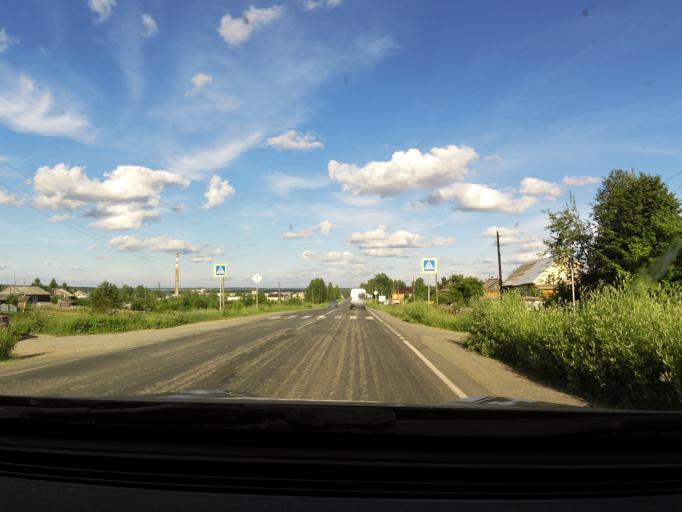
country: RU
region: Kirov
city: Omutninsk
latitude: 58.6925
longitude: 52.2080
